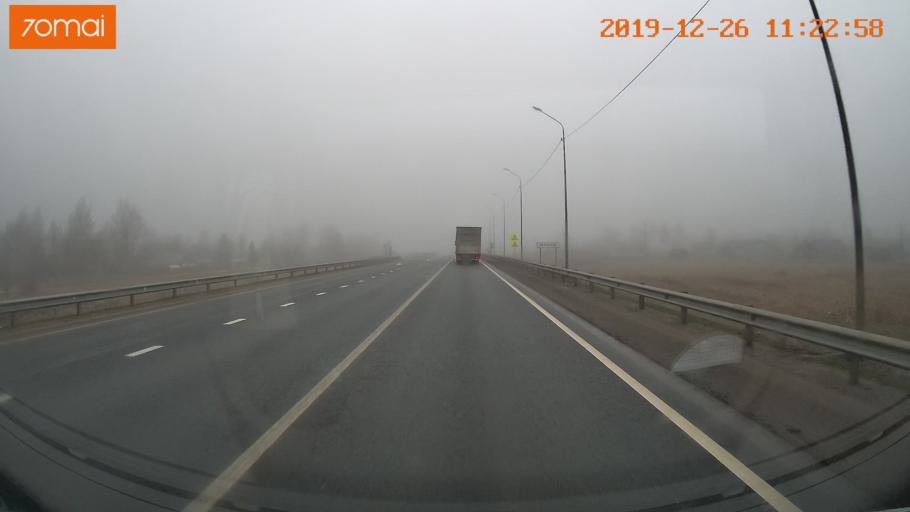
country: RU
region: Vologda
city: Chebsara
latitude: 59.1307
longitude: 38.9318
